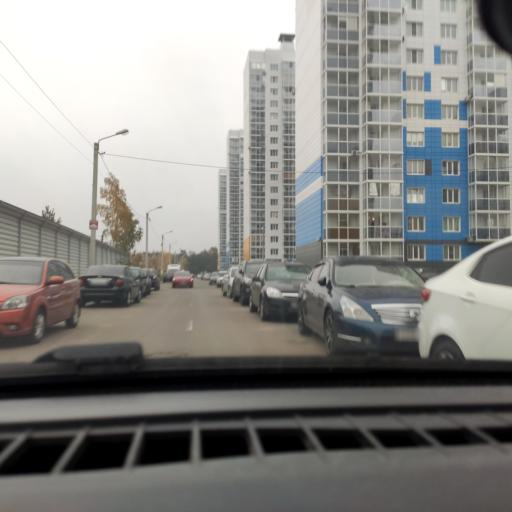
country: RU
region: Voronezj
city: Podgornoye
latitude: 51.7609
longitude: 39.1815
